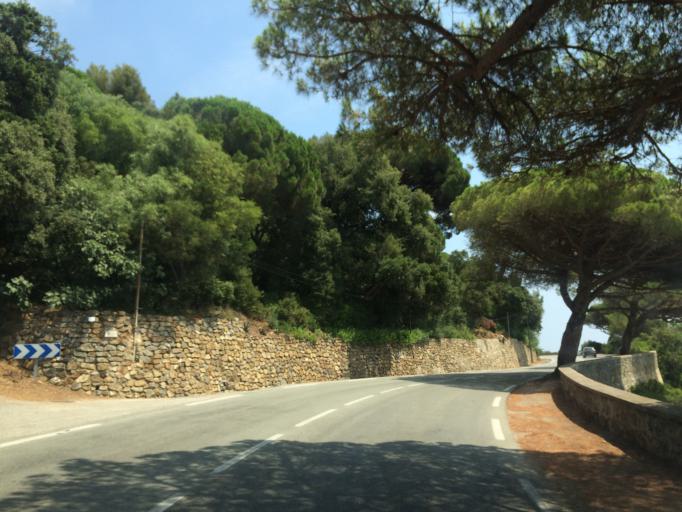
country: FR
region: Provence-Alpes-Cote d'Azur
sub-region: Departement du Var
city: Sainte-Maxime
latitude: 43.3143
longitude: 6.6616
